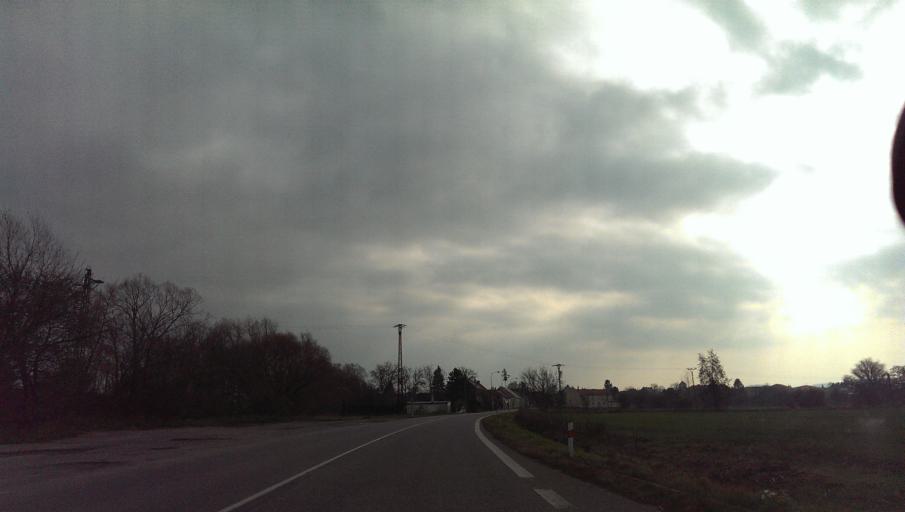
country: CZ
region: Zlin
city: Tlumacov
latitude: 49.2608
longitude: 17.4964
